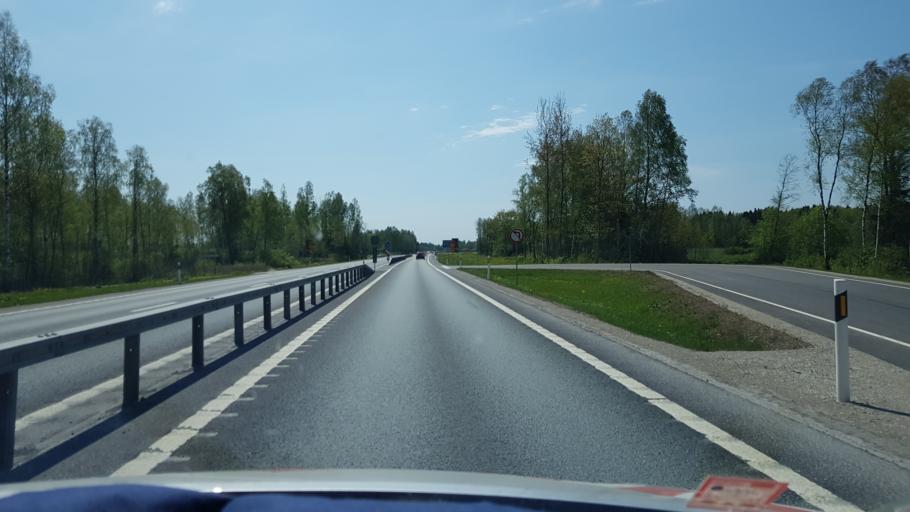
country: EE
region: Harju
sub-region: Saue linn
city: Saue
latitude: 59.1633
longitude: 24.5042
